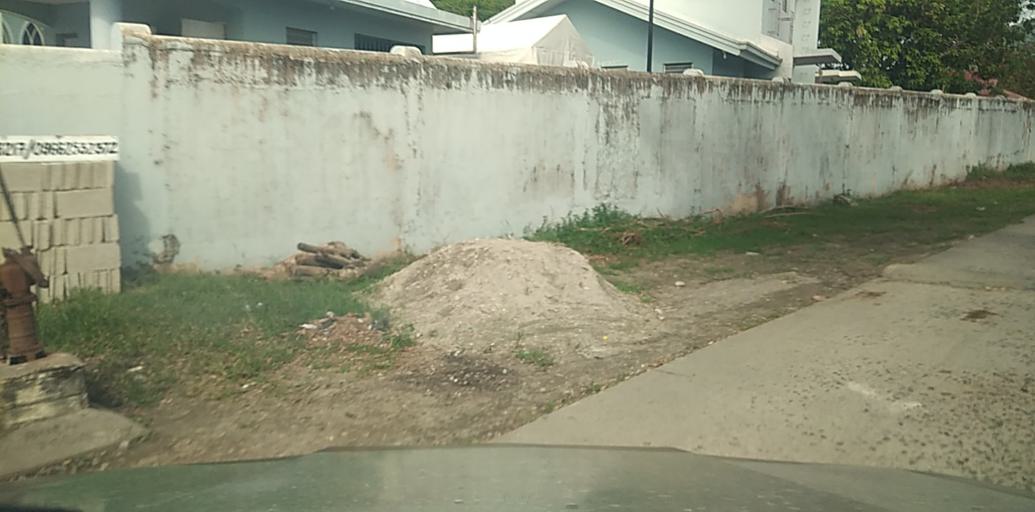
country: PH
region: Central Luzon
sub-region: Province of Pampanga
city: Buensuseso
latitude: 15.1925
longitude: 120.6737
